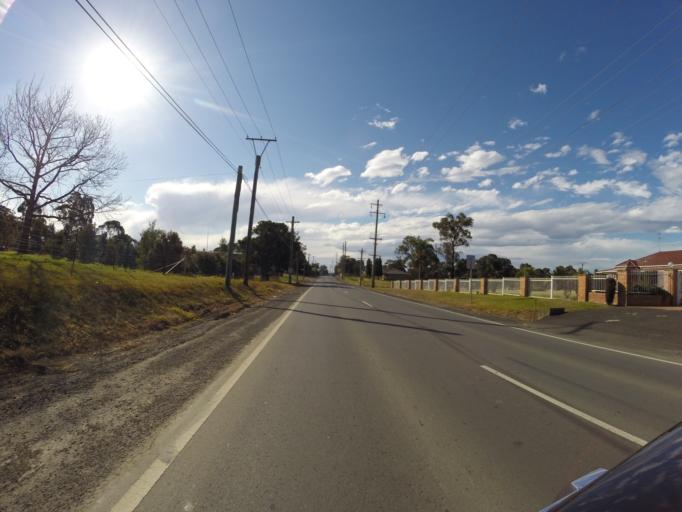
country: AU
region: New South Wales
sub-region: Fairfield
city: Cecil Park
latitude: -33.8848
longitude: 150.7919
